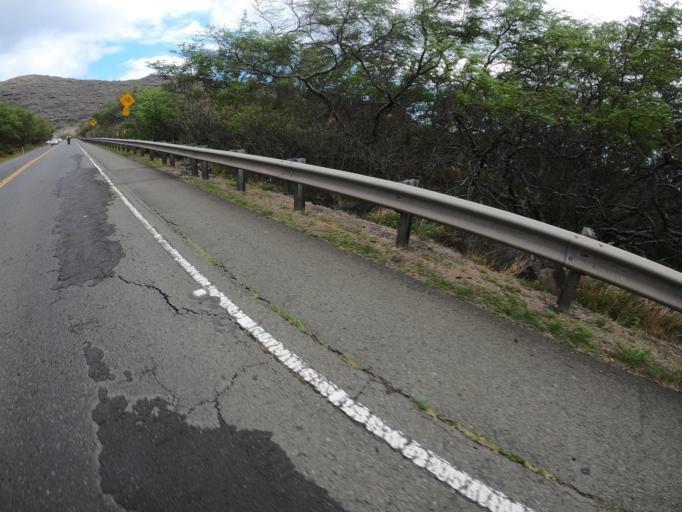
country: US
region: Hawaii
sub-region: Honolulu County
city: Waimanalo Beach
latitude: 21.3006
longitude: -157.6583
